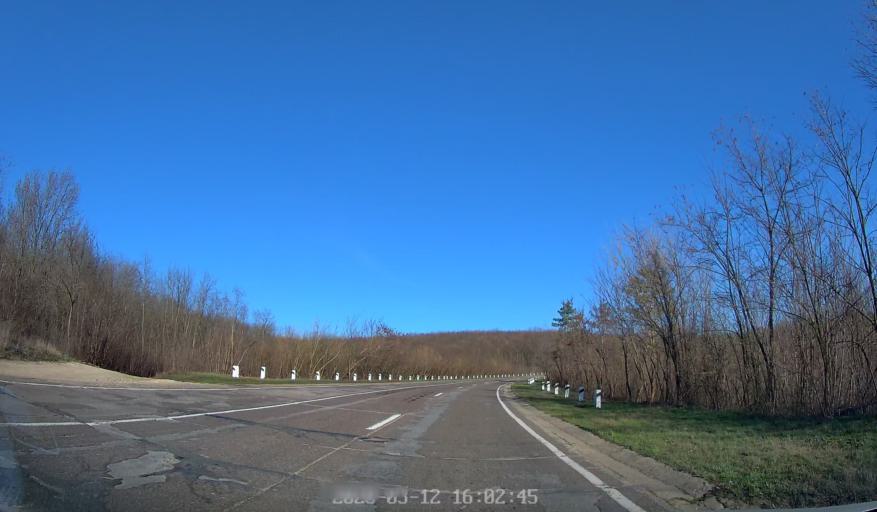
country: MD
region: Chisinau
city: Vadul lui Voda
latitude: 47.0322
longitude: 29.1472
